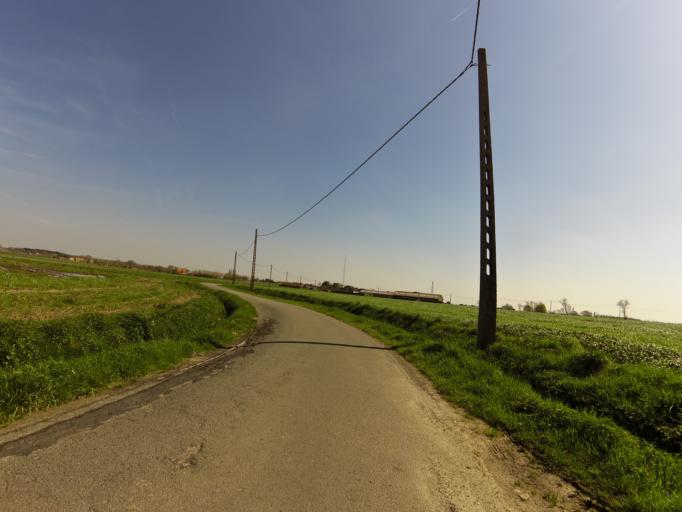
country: BE
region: Flanders
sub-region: Provincie West-Vlaanderen
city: Ichtegem
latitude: 51.0767
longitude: 3.0077
